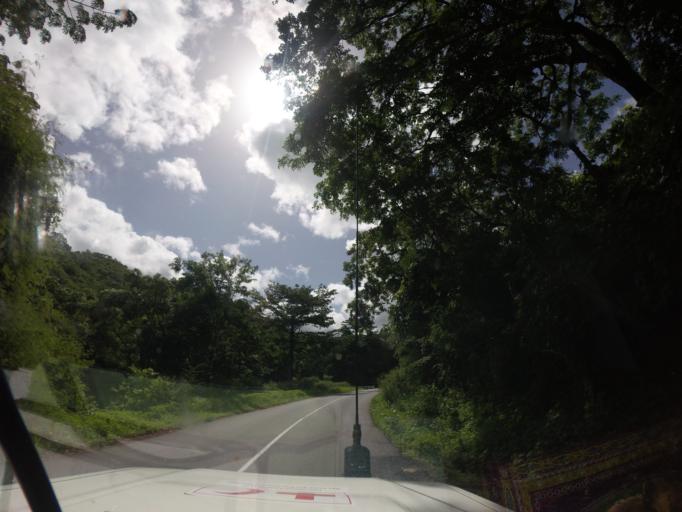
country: GN
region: Mamou
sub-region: Mamou Prefecture
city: Mamou
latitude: 10.2968
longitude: -11.9418
